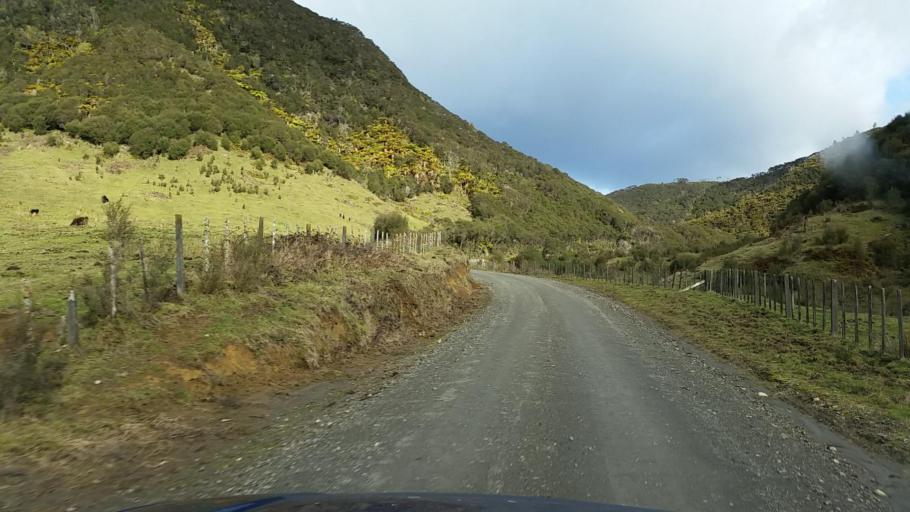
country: NZ
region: Taranaki
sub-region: South Taranaki District
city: Eltham
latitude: -39.2664
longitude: 174.7442
